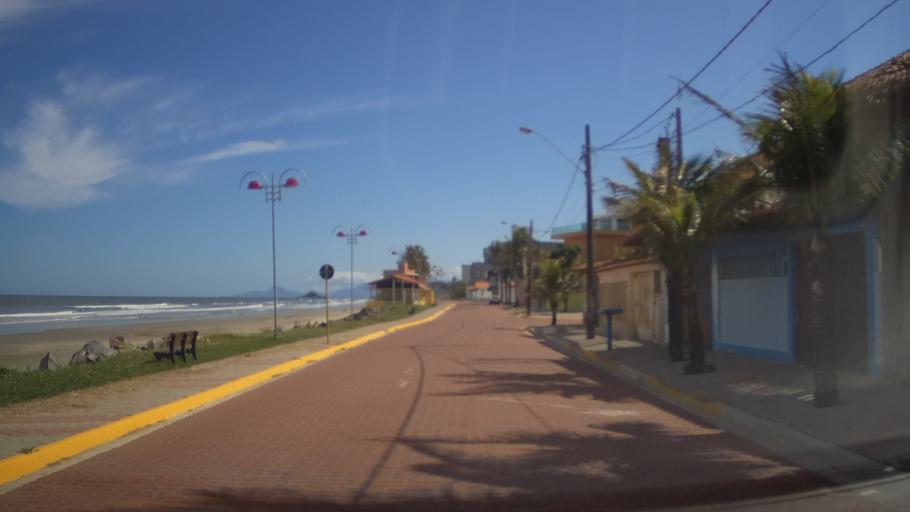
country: BR
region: Sao Paulo
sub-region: Itanhaem
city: Itanhaem
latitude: -24.1772
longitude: -46.7706
